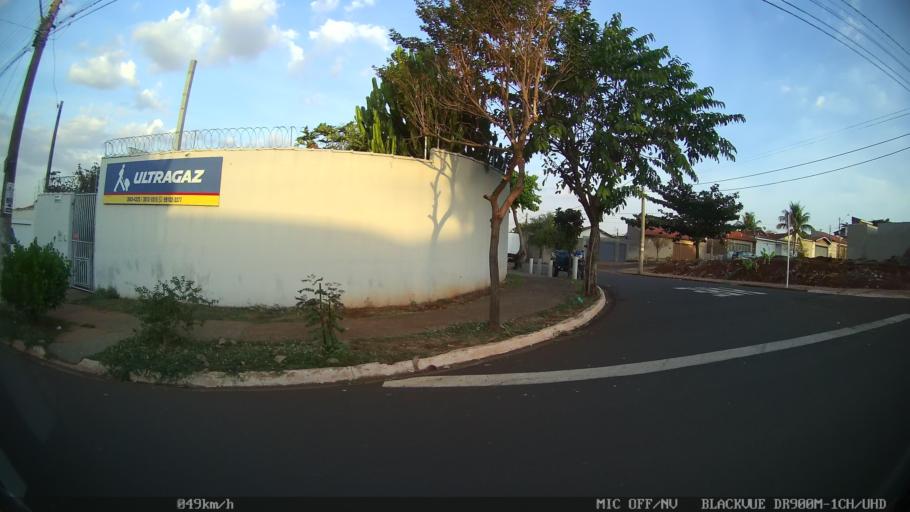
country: BR
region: Sao Paulo
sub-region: Ribeirao Preto
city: Ribeirao Preto
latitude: -21.1410
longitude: -47.8548
